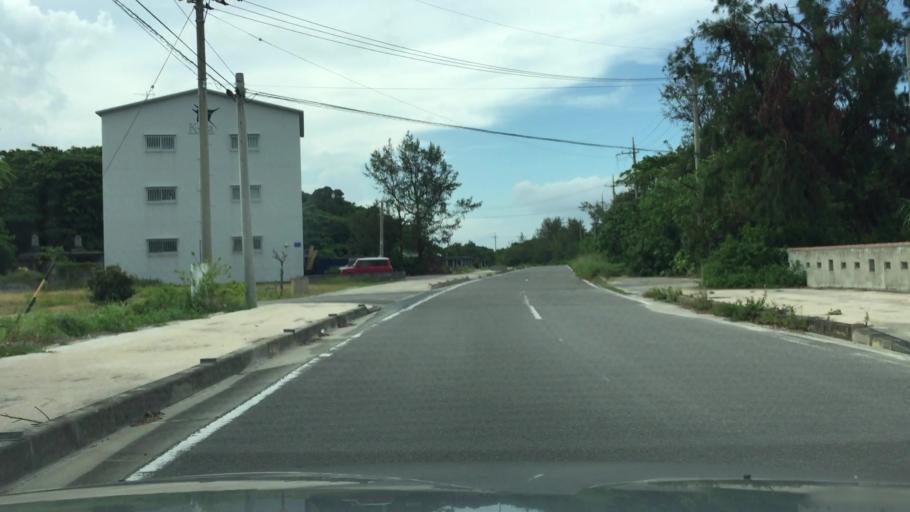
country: JP
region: Okinawa
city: Ishigaki
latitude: 24.4637
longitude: 124.1425
